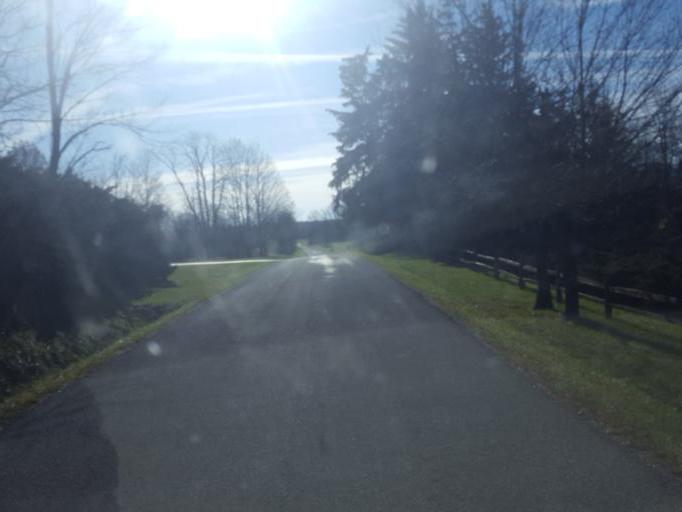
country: US
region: Ohio
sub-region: Richland County
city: Ontario
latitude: 40.8222
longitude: -82.5888
